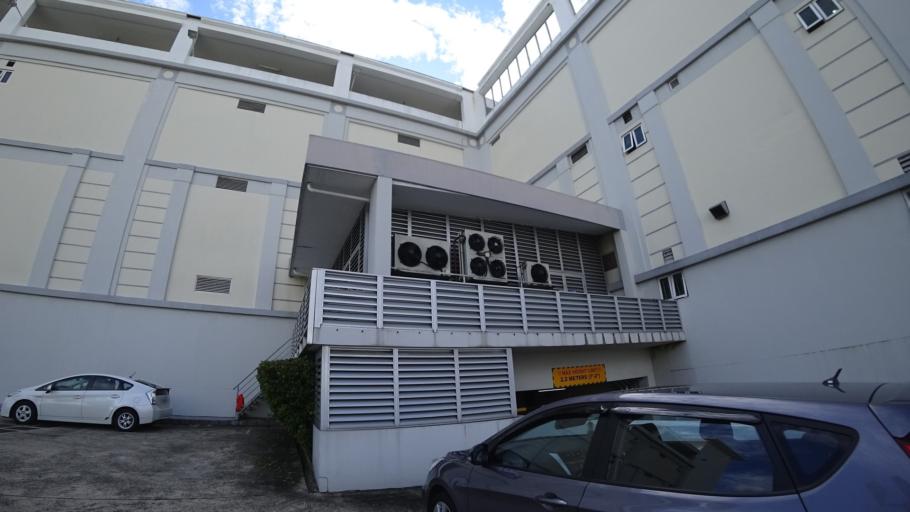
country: BN
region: Brunei and Muara
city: Bandar Seri Begawan
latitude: 4.8890
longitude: 114.8572
